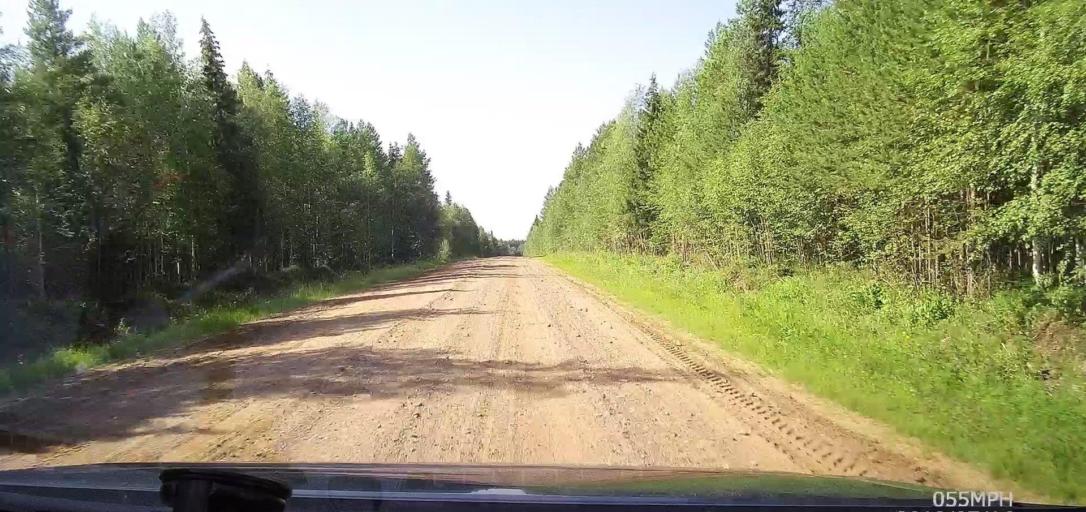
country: RU
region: Arkhangelskaya
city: Leshukonskoye
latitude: 65.4289
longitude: 45.0682
